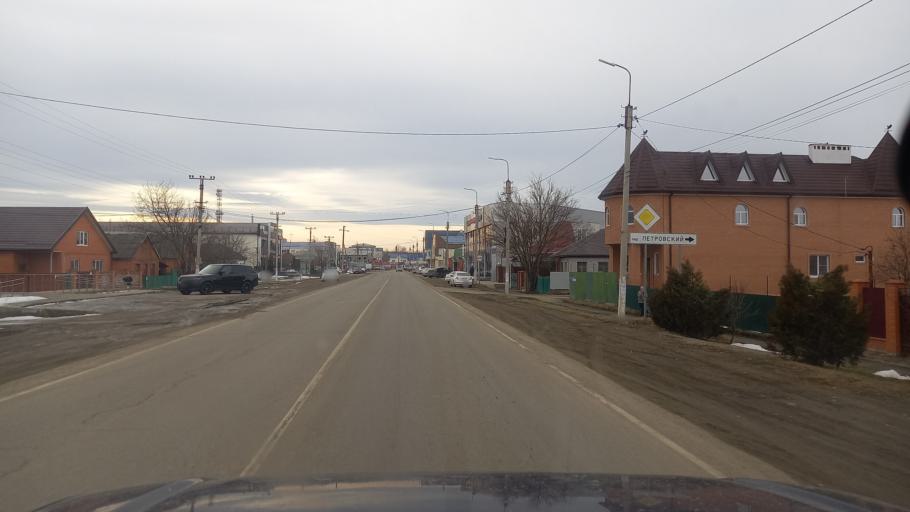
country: RU
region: Krasnodarskiy
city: Belorechensk
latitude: 44.7670
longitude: 39.8757
